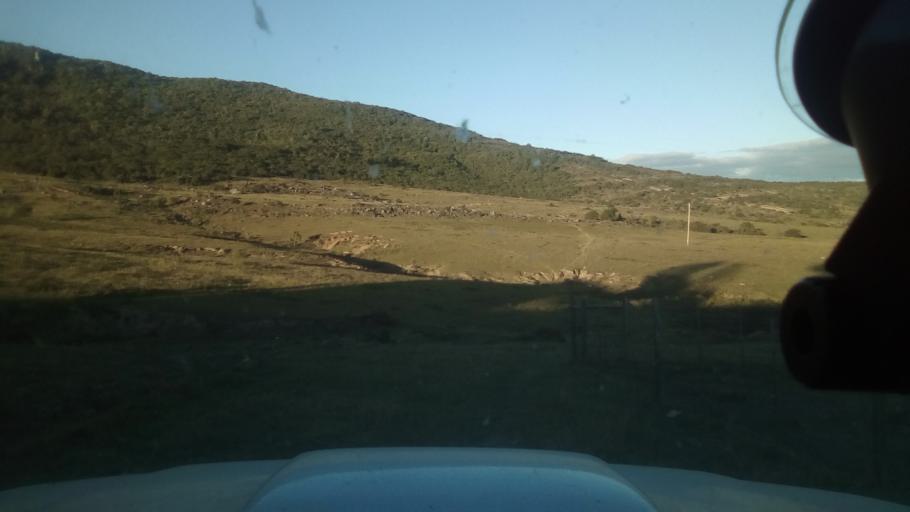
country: ZA
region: Eastern Cape
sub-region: Buffalo City Metropolitan Municipality
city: Bhisho
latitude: -32.7353
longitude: 27.3794
